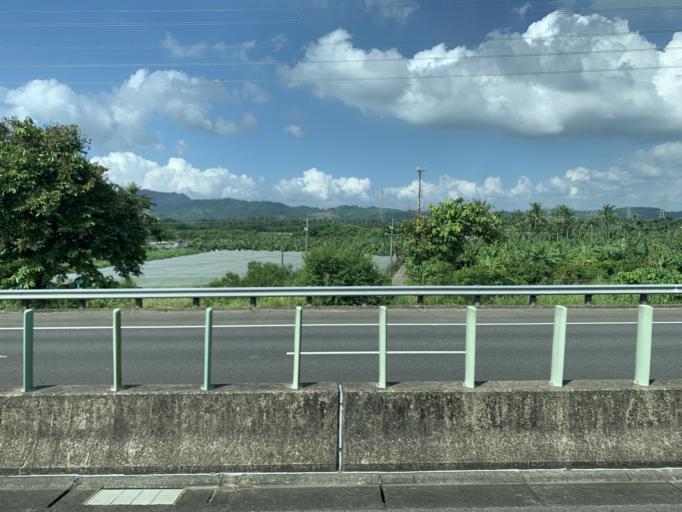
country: TW
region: Taiwan
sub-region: Pingtung
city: Pingtung
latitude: 22.8531
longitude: 120.4949
